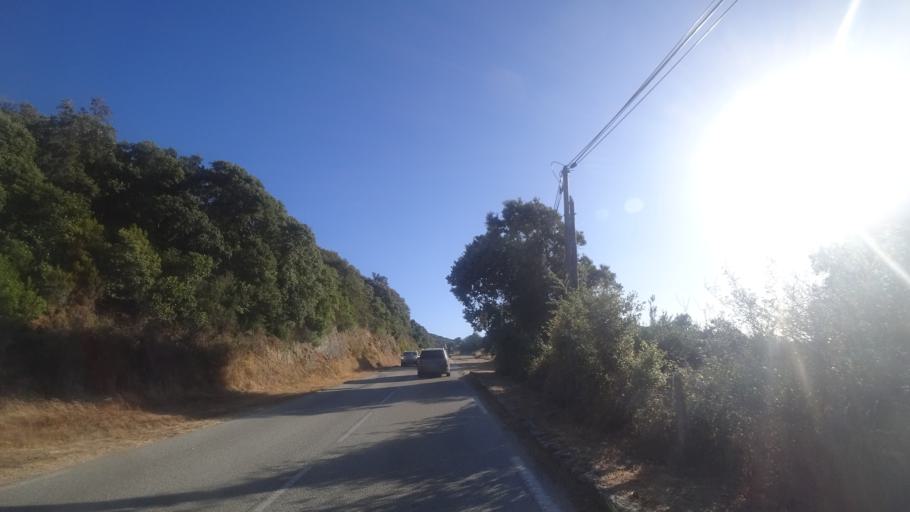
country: FR
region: Corsica
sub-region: Departement de la Corse-du-Sud
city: Cargese
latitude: 42.1671
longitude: 8.6042
